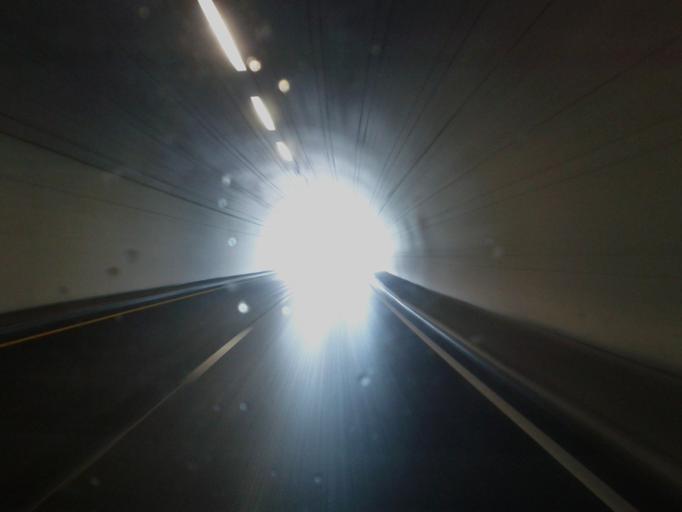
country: NO
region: Sor-Trondelag
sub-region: Melhus
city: Melhus
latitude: 63.2985
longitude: 10.2851
